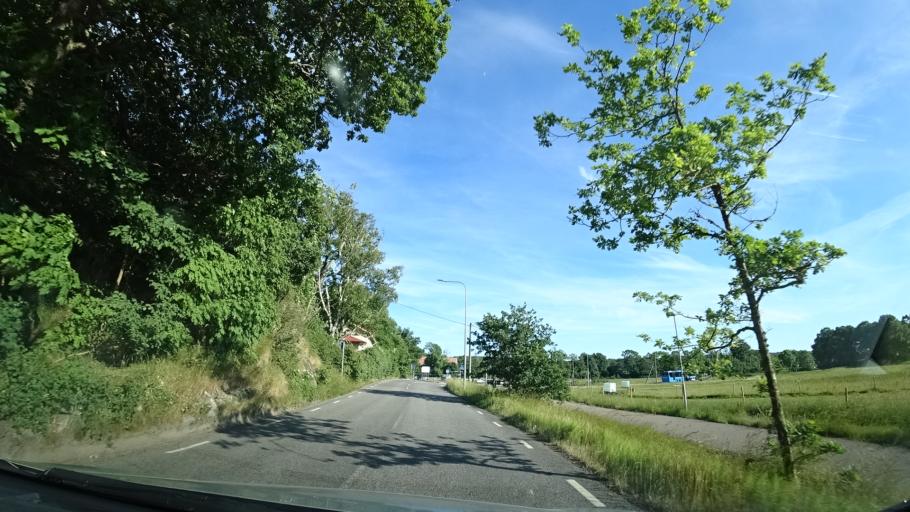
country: SE
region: Vaestra Goetaland
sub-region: Goteborg
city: Billdal
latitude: 57.5833
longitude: 11.9425
